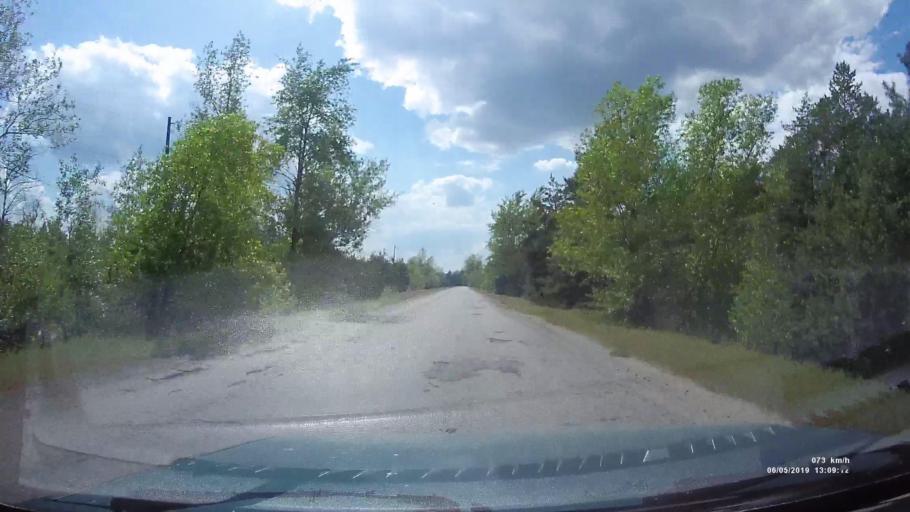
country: RU
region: Rostov
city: Ust'-Donetskiy
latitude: 47.7703
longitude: 40.9870
